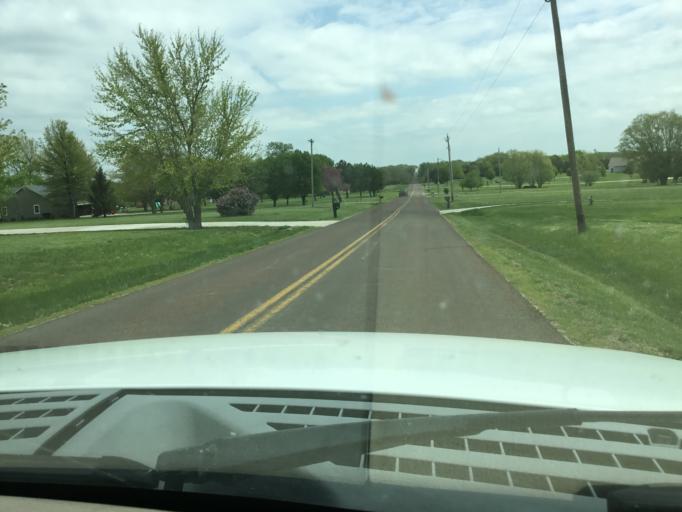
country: US
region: Kansas
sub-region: Shawnee County
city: Auburn
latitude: 38.9707
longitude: -95.7946
